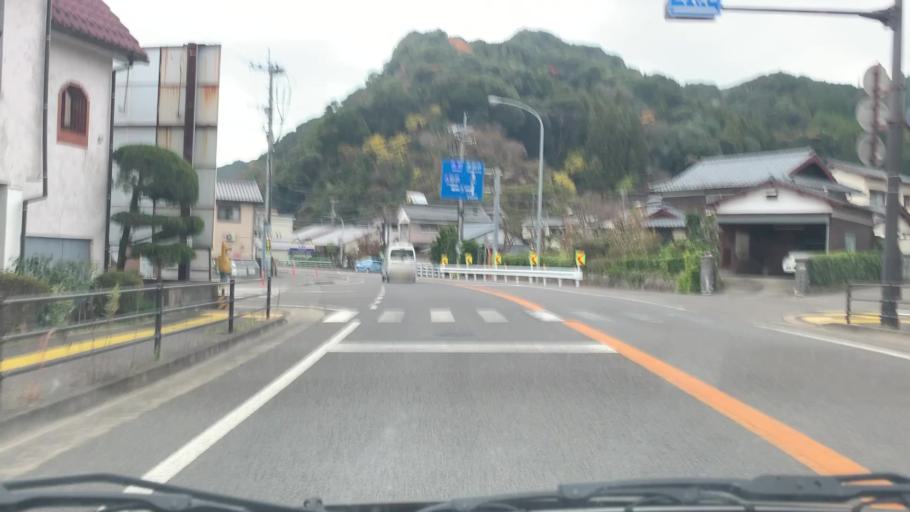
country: JP
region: Saga Prefecture
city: Ureshinomachi-shimojuku
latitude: 33.0942
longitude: 129.9774
